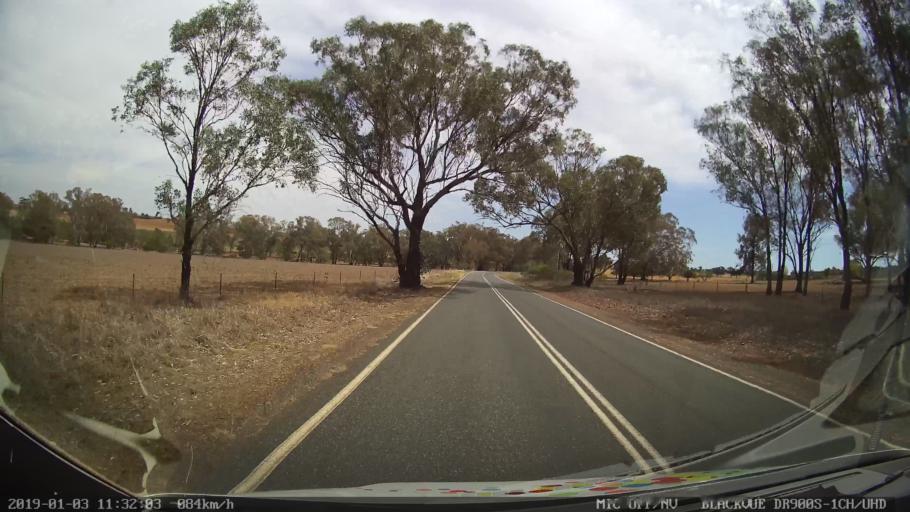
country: AU
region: New South Wales
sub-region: Weddin
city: Grenfell
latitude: -33.9632
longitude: 148.1806
